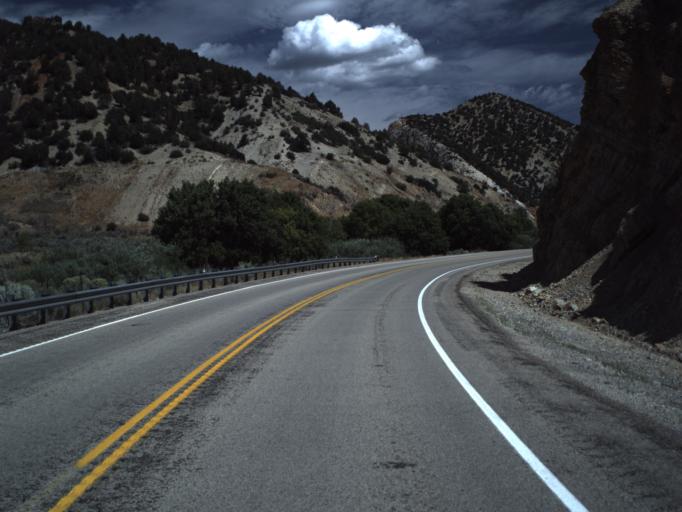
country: US
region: Utah
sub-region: Utah County
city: Woodland Hills
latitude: 39.9843
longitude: -111.5022
